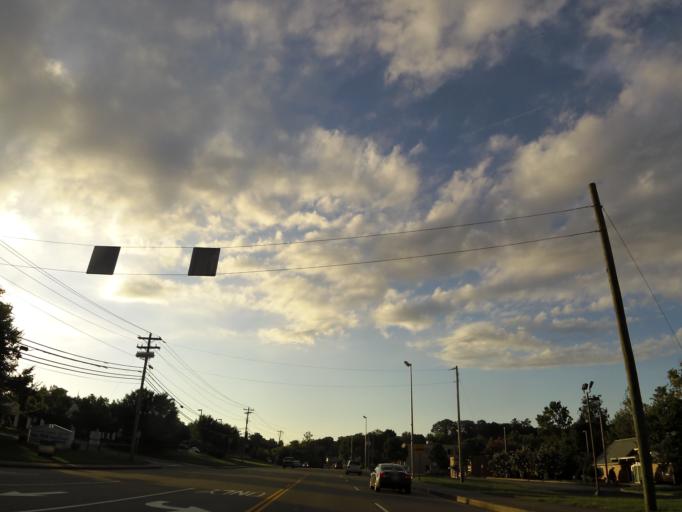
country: US
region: Tennessee
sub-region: Knox County
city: Farragut
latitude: 35.8819
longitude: -84.1609
